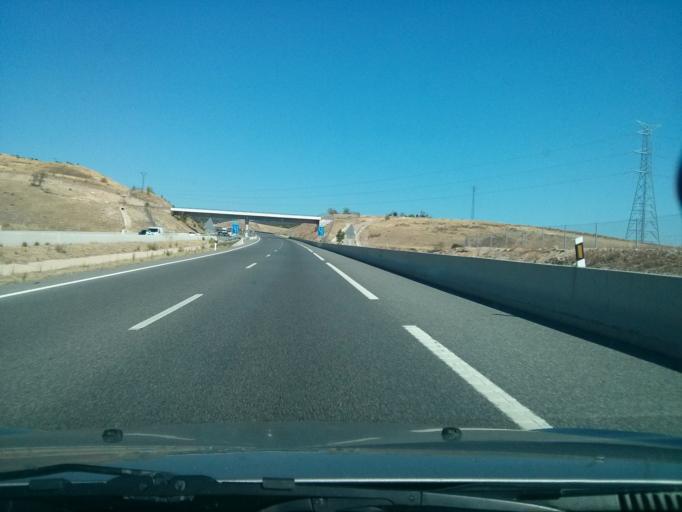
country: ES
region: Madrid
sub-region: Provincia de Madrid
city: El Molar
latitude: 40.7370
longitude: -3.5674
